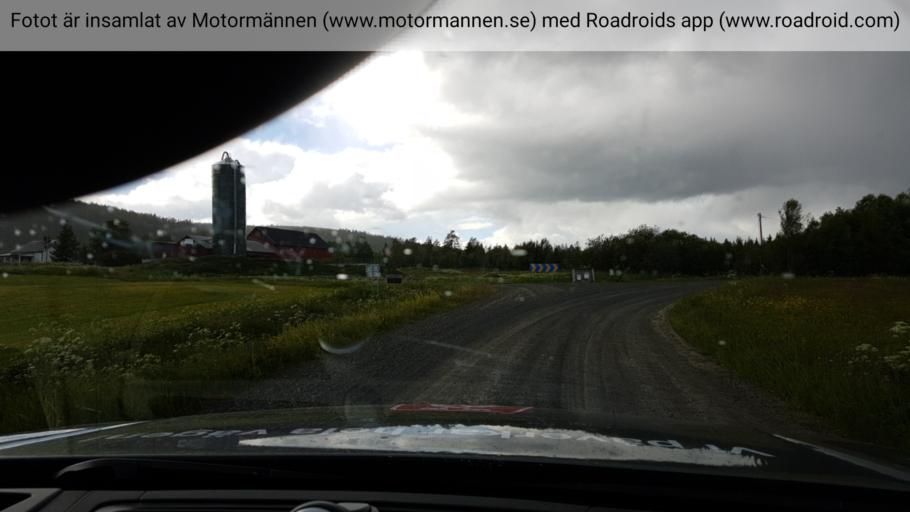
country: SE
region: Jaemtland
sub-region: Bergs Kommun
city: Hoverberg
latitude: 62.9608
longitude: 14.2382
